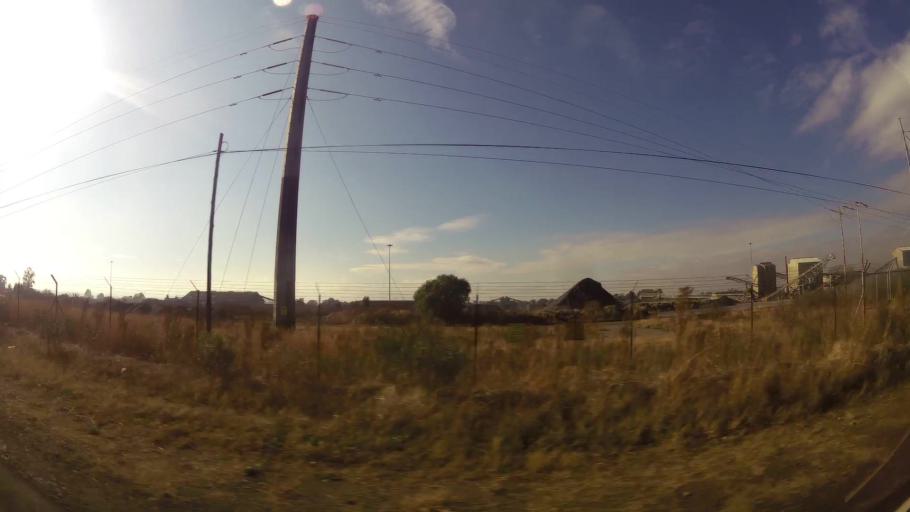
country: ZA
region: Gauteng
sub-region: Sedibeng District Municipality
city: Meyerton
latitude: -26.5079
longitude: 28.0554
